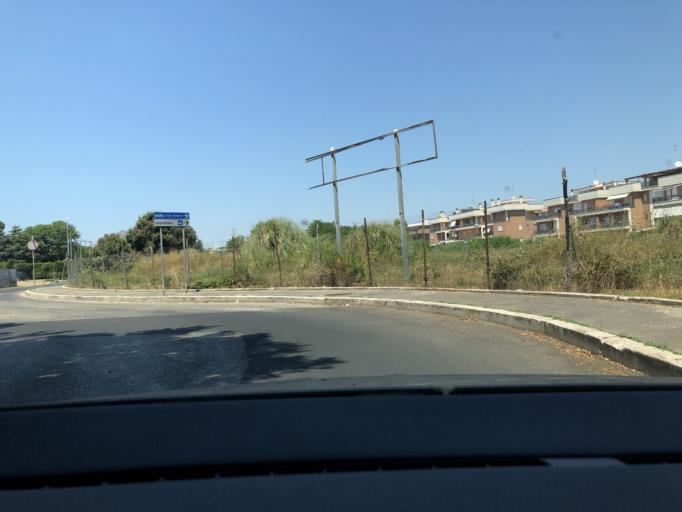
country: IT
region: Latium
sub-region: Citta metropolitana di Roma Capitale
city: Anzio
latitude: 41.4589
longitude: 12.6417
